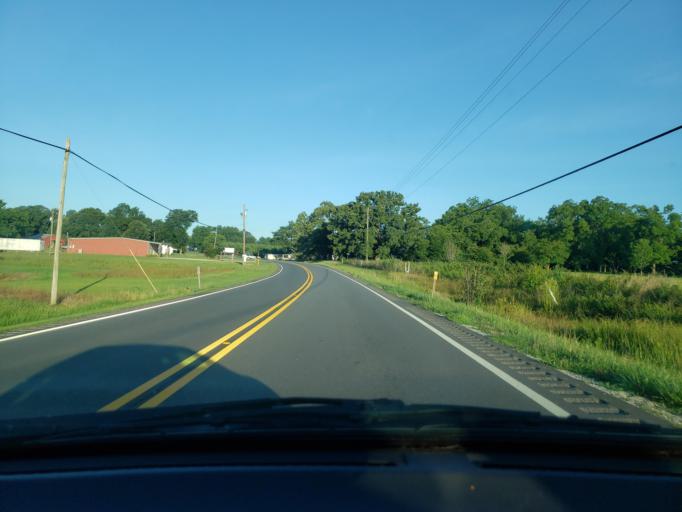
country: US
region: Alabama
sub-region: Elmore County
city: Tallassee
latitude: 32.5827
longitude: -85.7450
